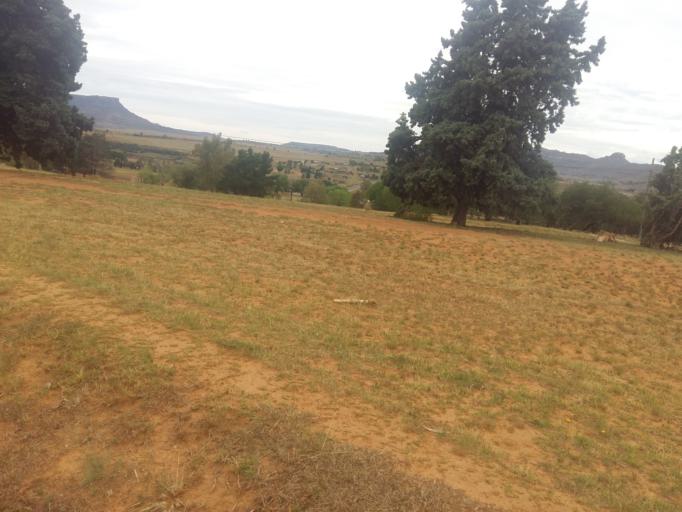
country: LS
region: Mafeteng
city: Mafeteng
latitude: -29.6948
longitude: 27.4328
